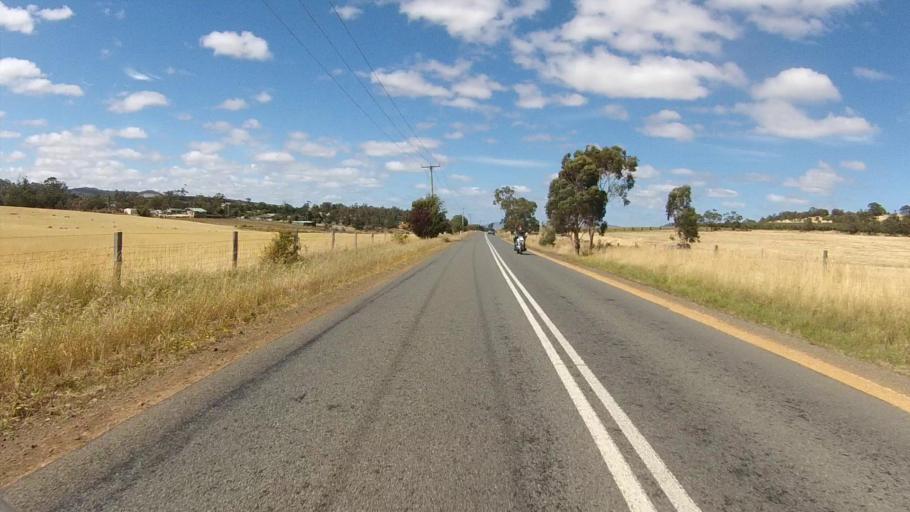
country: AU
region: Tasmania
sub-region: Sorell
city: Sorell
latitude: -42.6410
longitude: 147.4335
